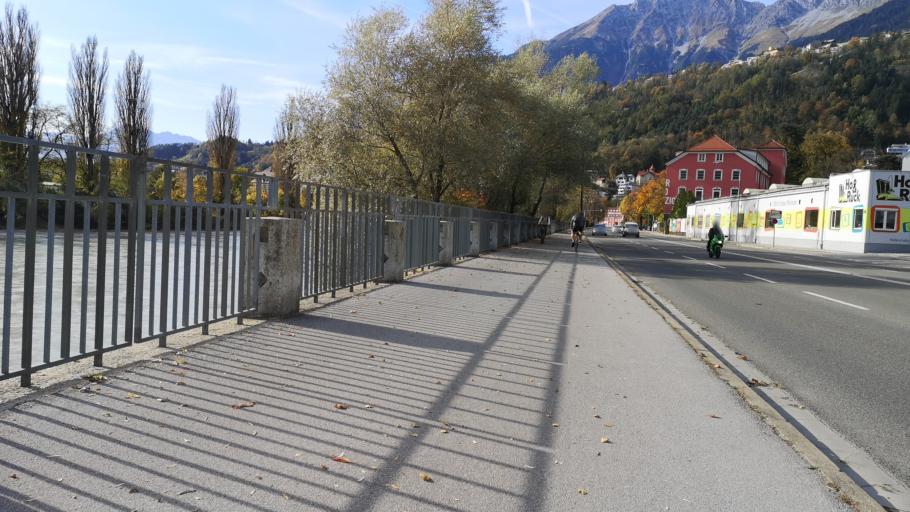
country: AT
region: Tyrol
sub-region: Innsbruck Stadt
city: Innsbruck
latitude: 47.2797
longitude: 11.4133
